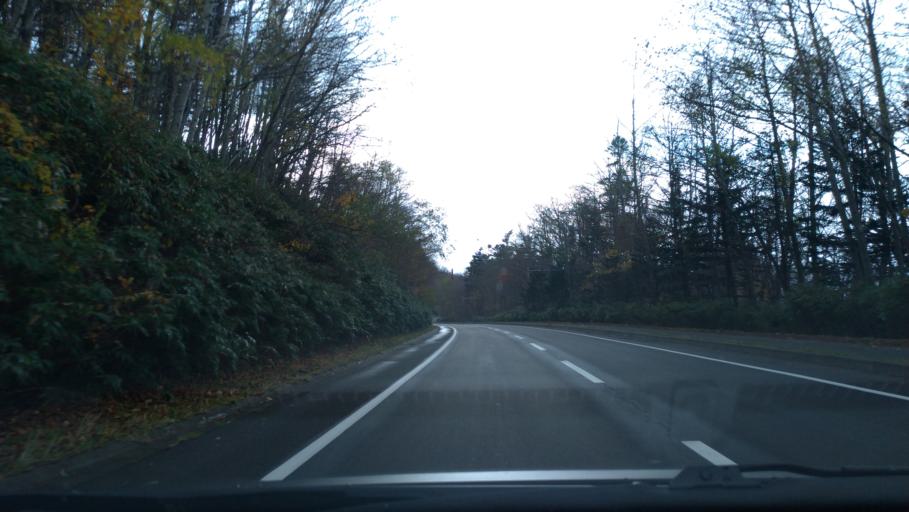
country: JP
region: Hokkaido
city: Shiraoi
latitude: 42.7312
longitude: 141.3386
